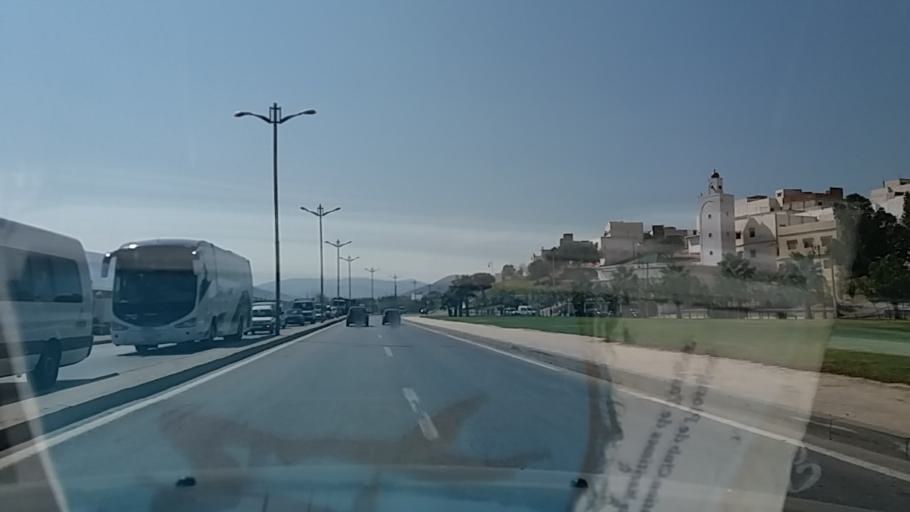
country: MA
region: Tanger-Tetouan
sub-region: Tetouan
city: Saddina
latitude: 35.5635
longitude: -5.4263
